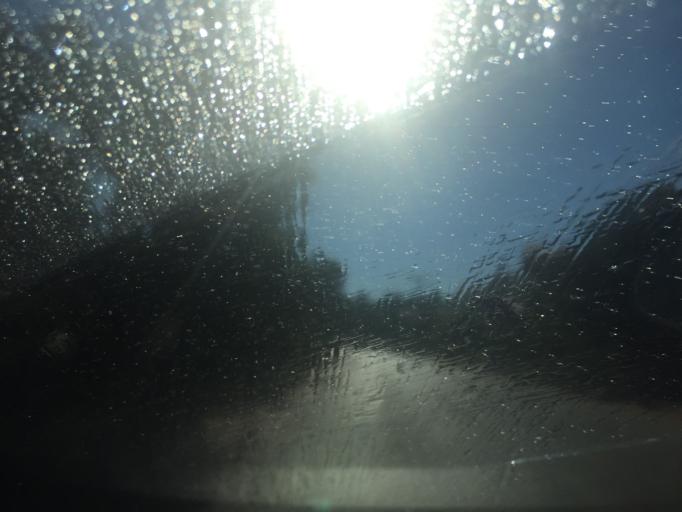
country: TH
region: Kalasin
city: Tha Khantho
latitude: 16.9790
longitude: 103.2629
